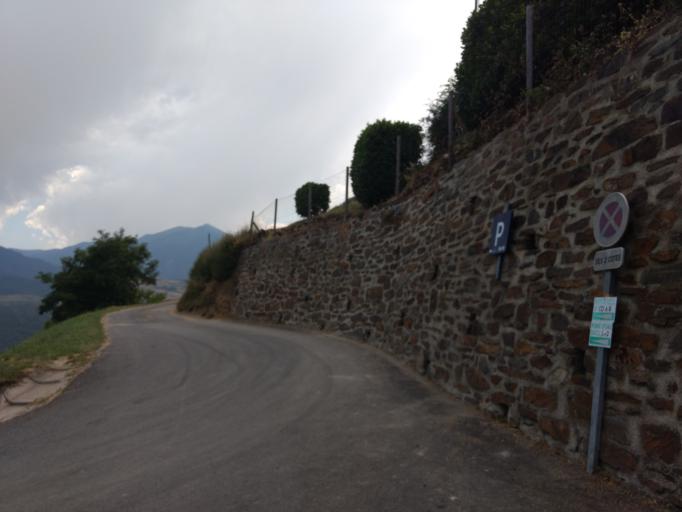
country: FR
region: Languedoc-Roussillon
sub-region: Departement des Pyrenees-Orientales
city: Vernet-les-Bains
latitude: 42.5699
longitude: 2.2954
